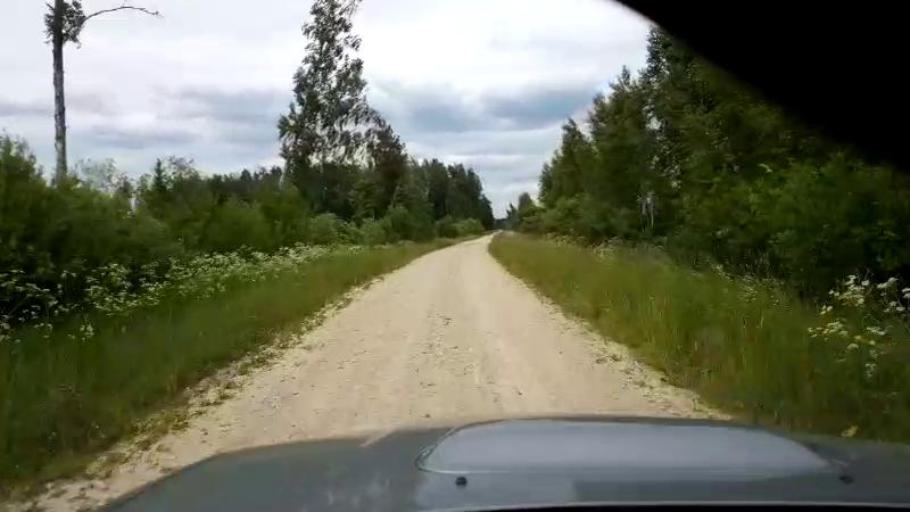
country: EE
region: Paernumaa
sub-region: Sauga vald
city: Sauga
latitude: 58.5047
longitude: 24.5804
